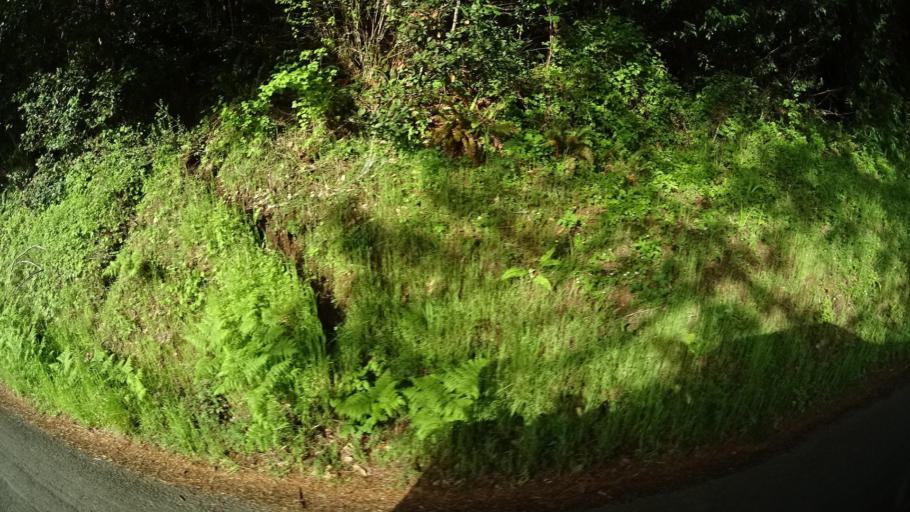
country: US
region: California
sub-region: Humboldt County
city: Blue Lake
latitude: 40.8793
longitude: -124.0150
